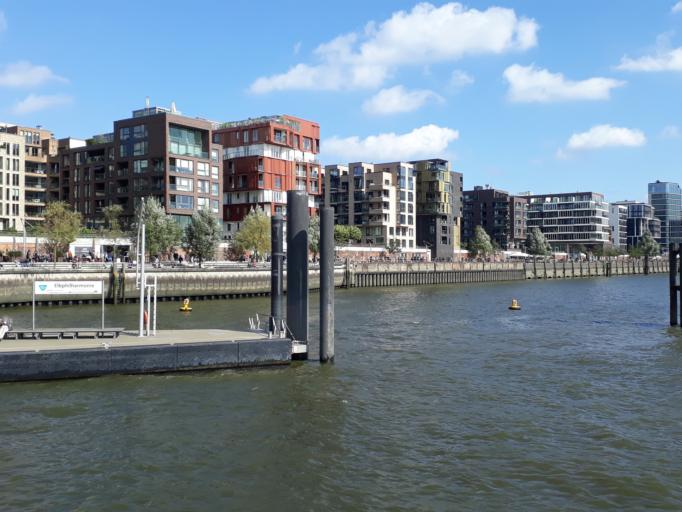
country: DE
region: Hamburg
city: Kleiner Grasbrook
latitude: 53.5399
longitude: 9.9866
